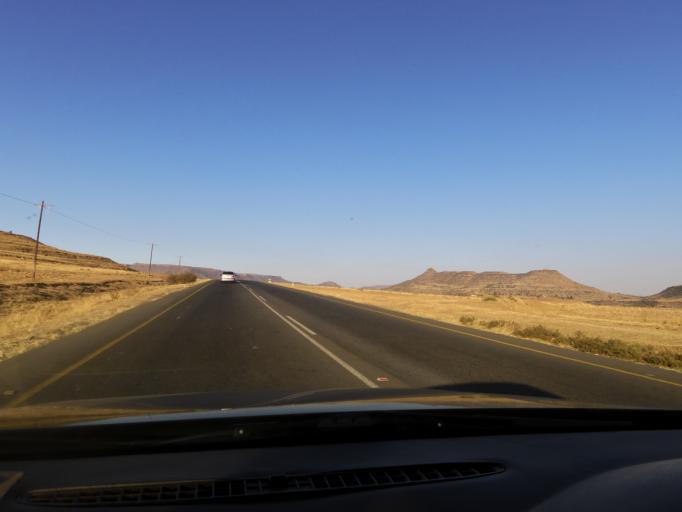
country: LS
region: Maseru
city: Maseru
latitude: -29.5281
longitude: 27.5175
